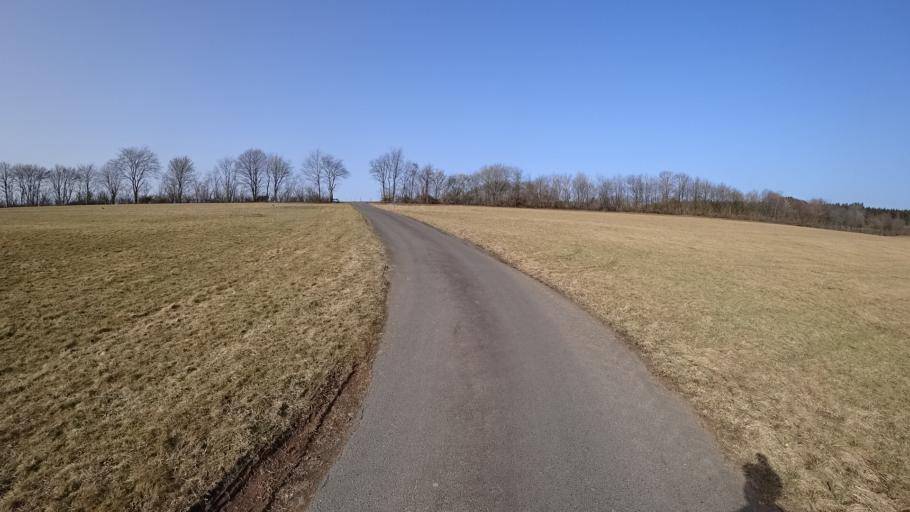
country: DE
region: Rheinland-Pfalz
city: Dickendorf
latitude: 50.7317
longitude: 7.8425
